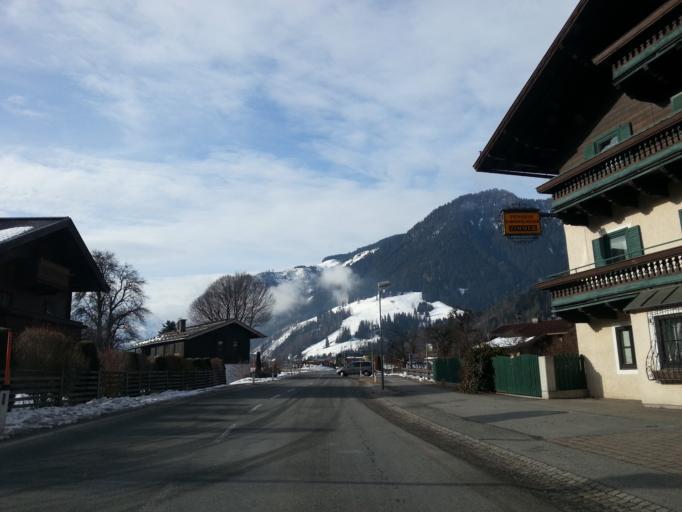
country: AT
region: Salzburg
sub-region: Politischer Bezirk Zell am See
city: Maishofen
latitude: 47.3683
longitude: 12.8047
